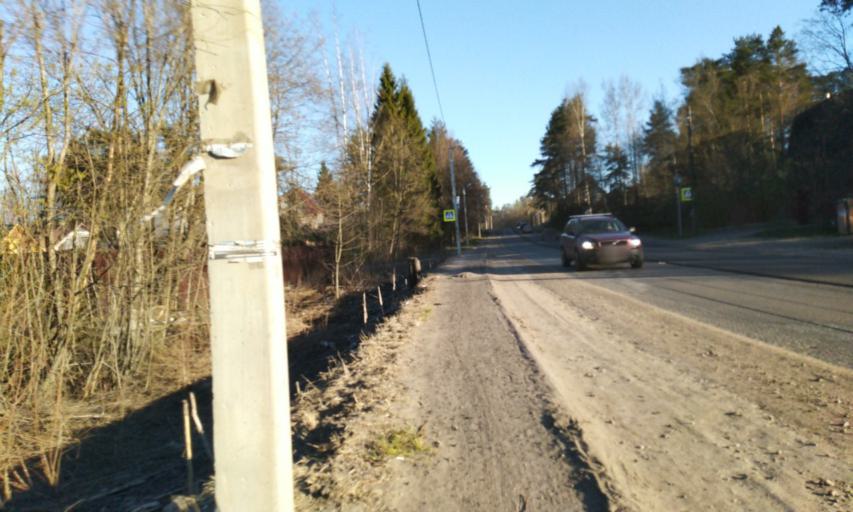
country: RU
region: Leningrad
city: Toksovo
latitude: 60.1430
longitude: 30.5287
